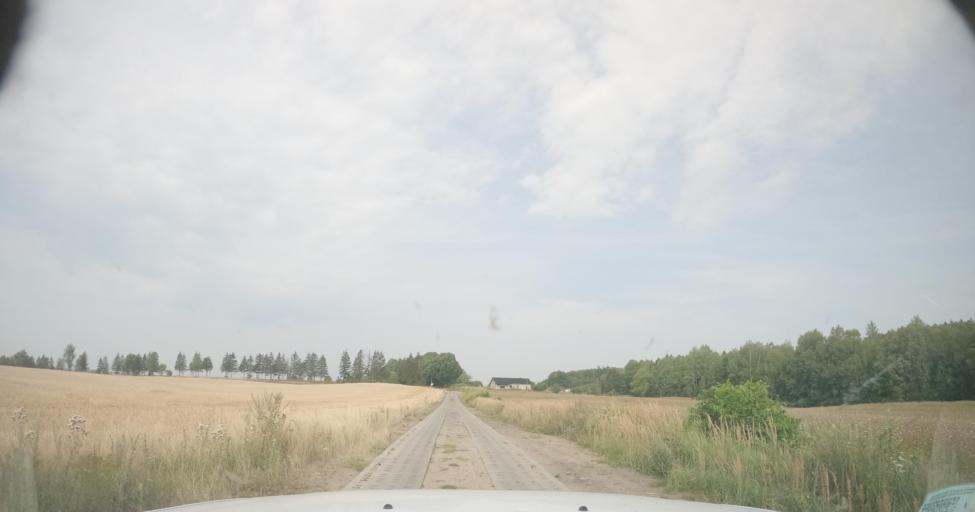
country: PL
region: West Pomeranian Voivodeship
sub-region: Powiat drawski
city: Czaplinek
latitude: 53.5756
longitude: 16.2750
